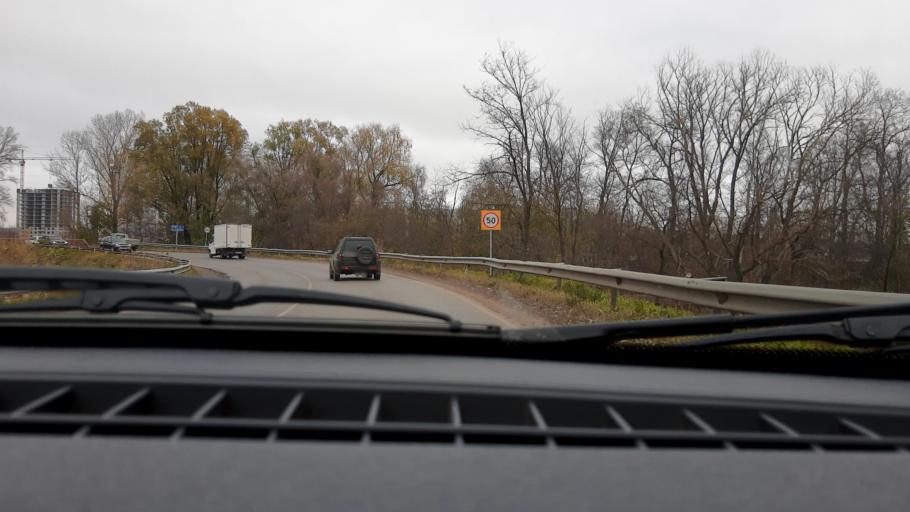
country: RU
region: Bashkortostan
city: Mikhaylovka
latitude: 54.7874
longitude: 55.8417
